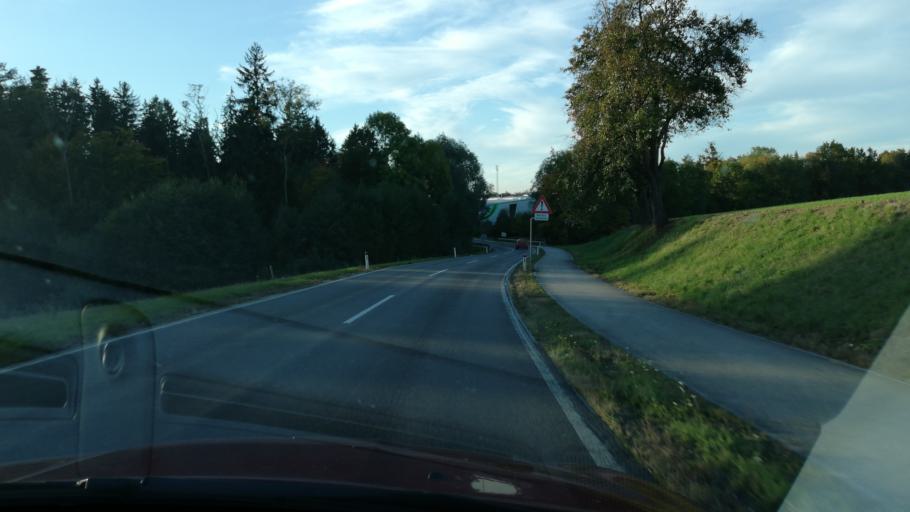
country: AT
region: Upper Austria
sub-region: Politischer Bezirk Steyr-Land
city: Waldneukirchen
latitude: 48.0050
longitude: 14.2538
